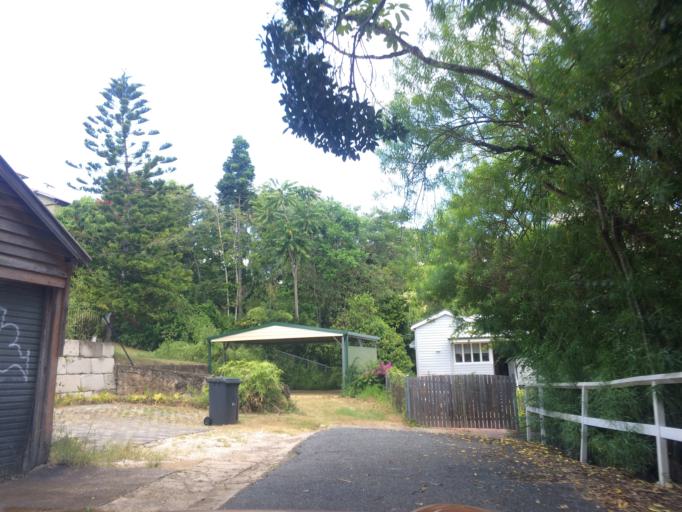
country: AU
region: Queensland
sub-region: Brisbane
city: Toowong
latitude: -27.4873
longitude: 153.0053
